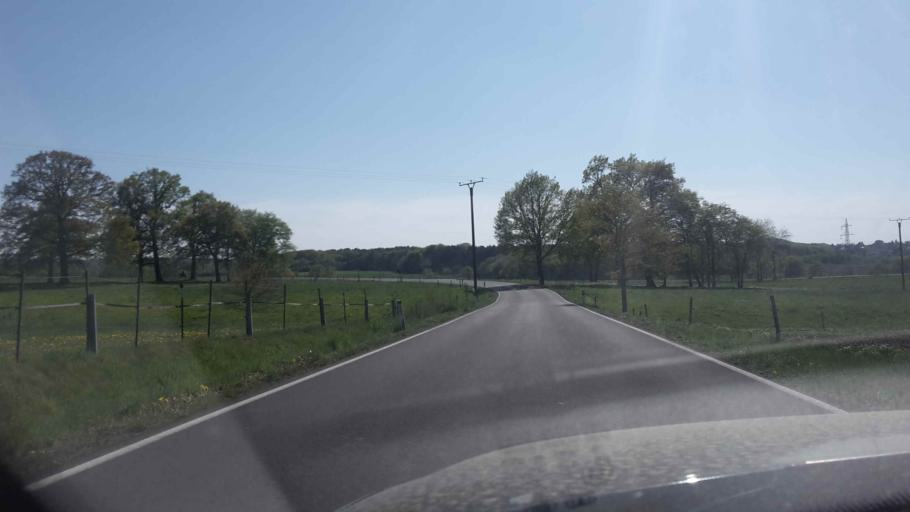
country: DE
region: Rheinland-Pfalz
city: Windhagen
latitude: 50.6778
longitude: 7.3341
